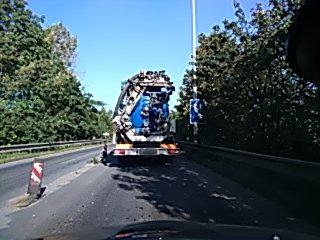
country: CZ
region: Pardubicky
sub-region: Okres Pardubice
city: Pardubice
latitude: 50.0365
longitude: 15.7476
